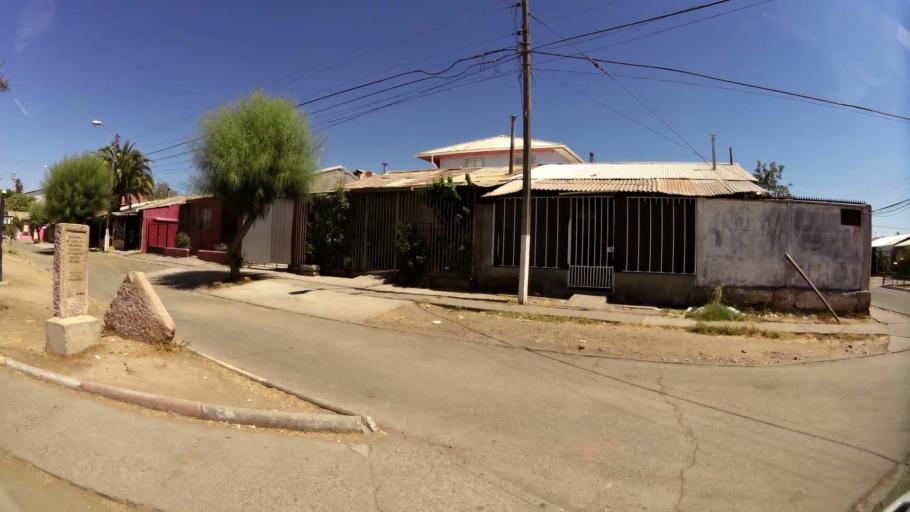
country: CL
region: O'Higgins
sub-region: Provincia de Colchagua
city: Chimbarongo
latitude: -34.5759
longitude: -70.9889
